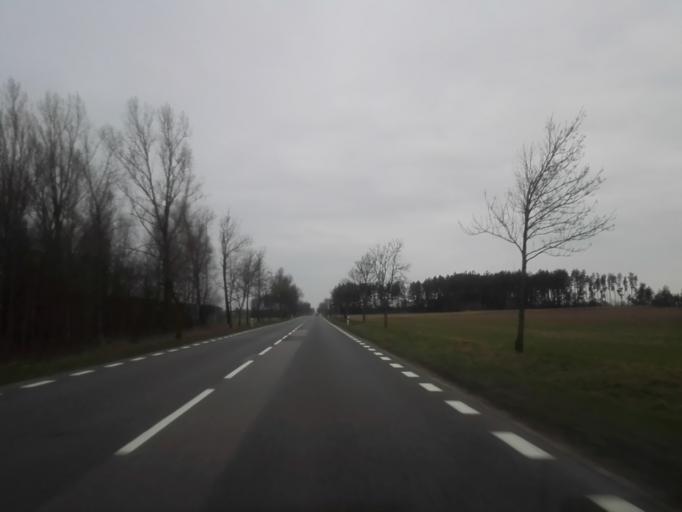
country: PL
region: Podlasie
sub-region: Powiat kolnenski
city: Stawiski
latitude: 53.4737
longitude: 22.2079
